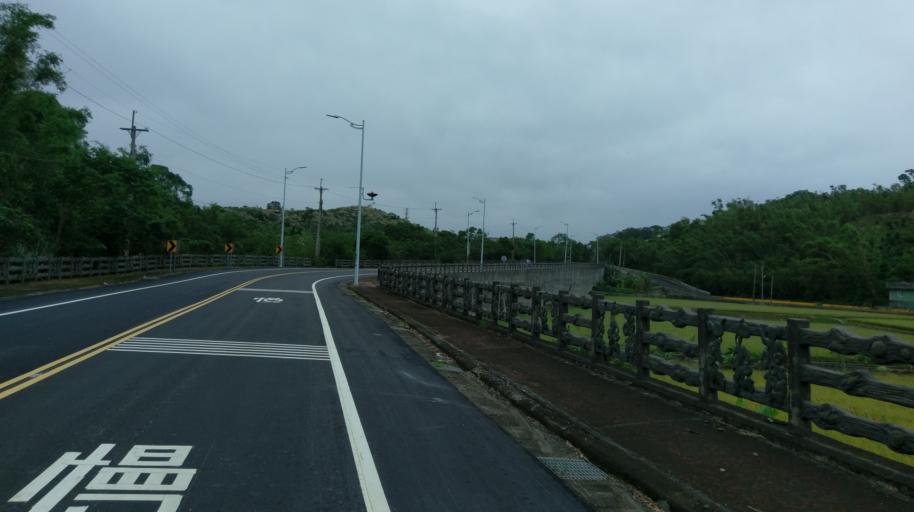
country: TW
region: Taiwan
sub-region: Hsinchu
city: Hsinchu
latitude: 24.7225
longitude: 120.9258
